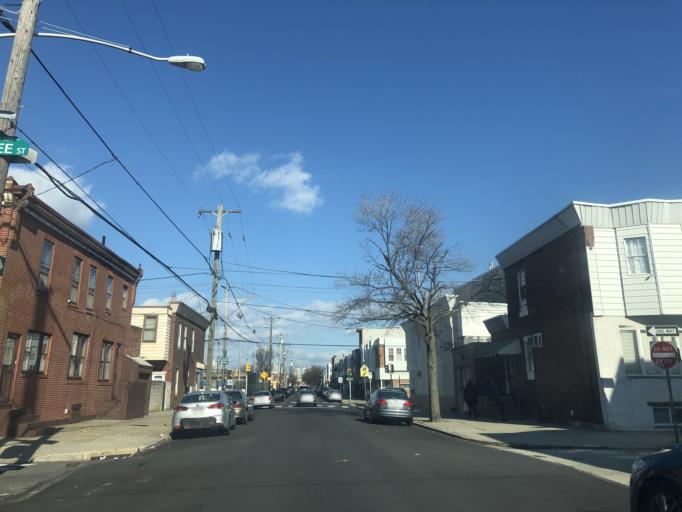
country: US
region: New Jersey
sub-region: Camden County
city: Camden
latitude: 39.9200
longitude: -75.1504
